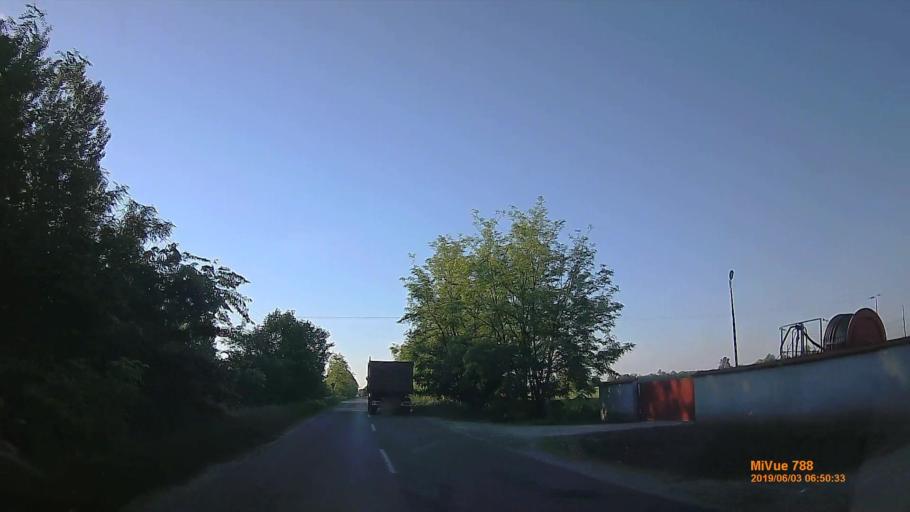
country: HU
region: Pest
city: Bugyi
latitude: 47.2191
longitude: 19.1736
